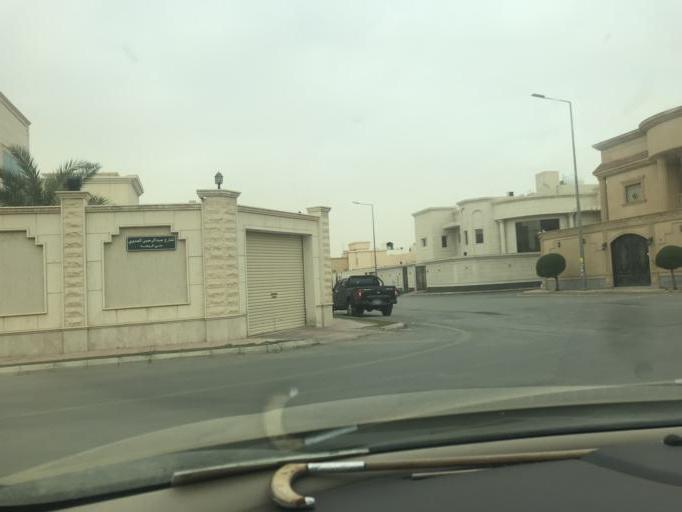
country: SA
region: Ar Riyad
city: Riyadh
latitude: 24.7356
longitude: 46.7578
